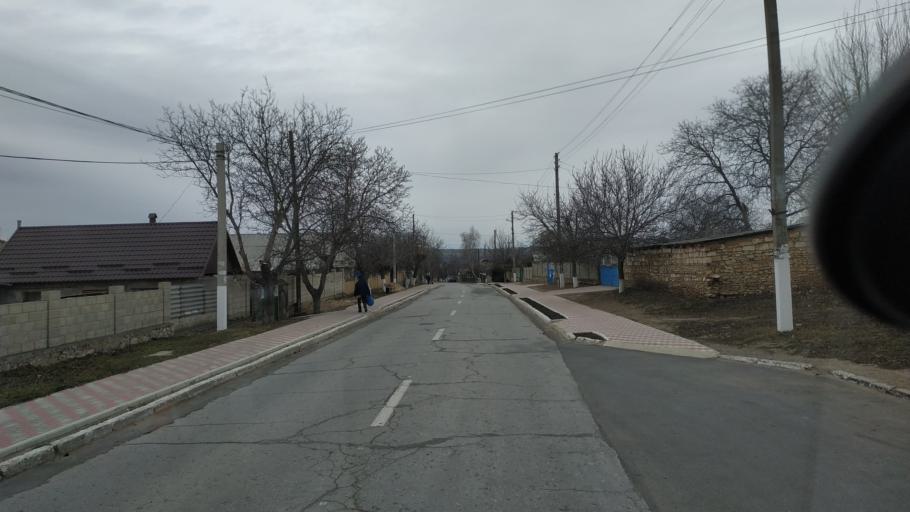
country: MD
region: Telenesti
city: Cocieri
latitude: 47.3403
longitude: 29.0963
